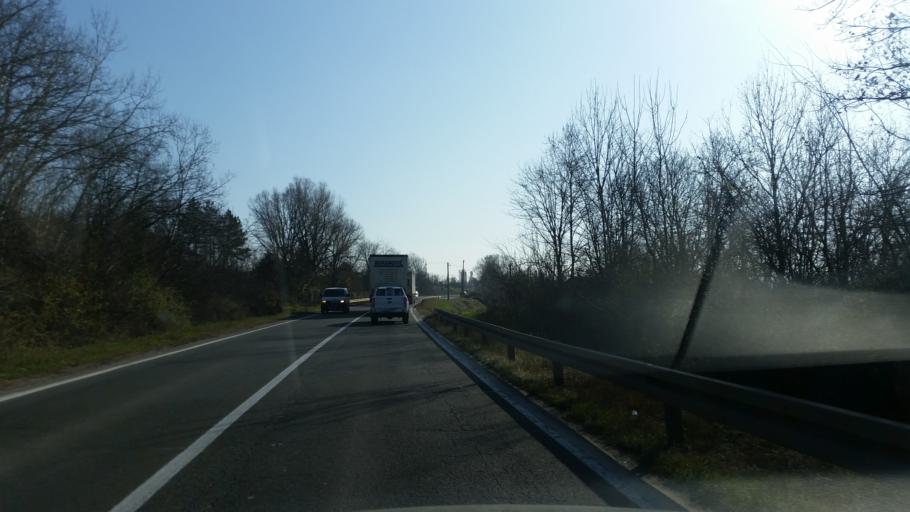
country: RS
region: Central Serbia
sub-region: Kolubarski Okrug
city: Ljig
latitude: 44.3063
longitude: 20.2550
